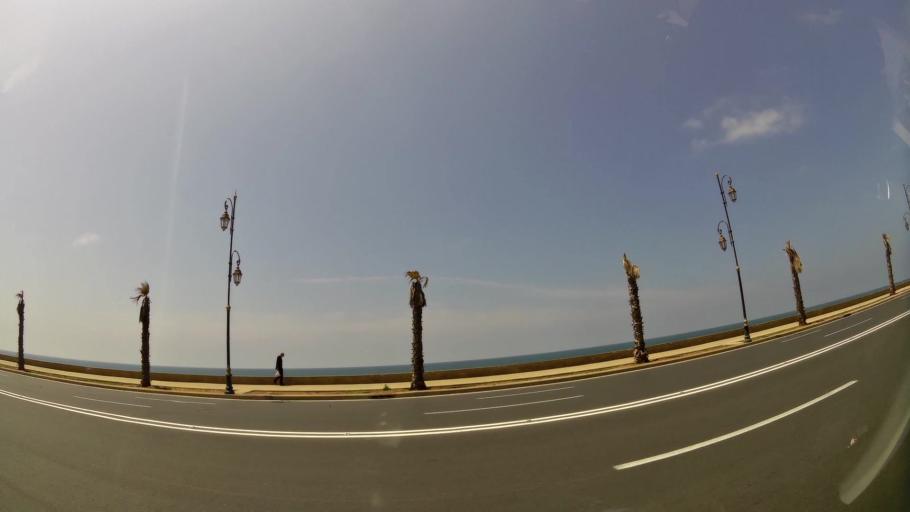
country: MA
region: Rabat-Sale-Zemmour-Zaer
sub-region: Rabat
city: Rabat
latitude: 34.0160
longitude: -6.8606
